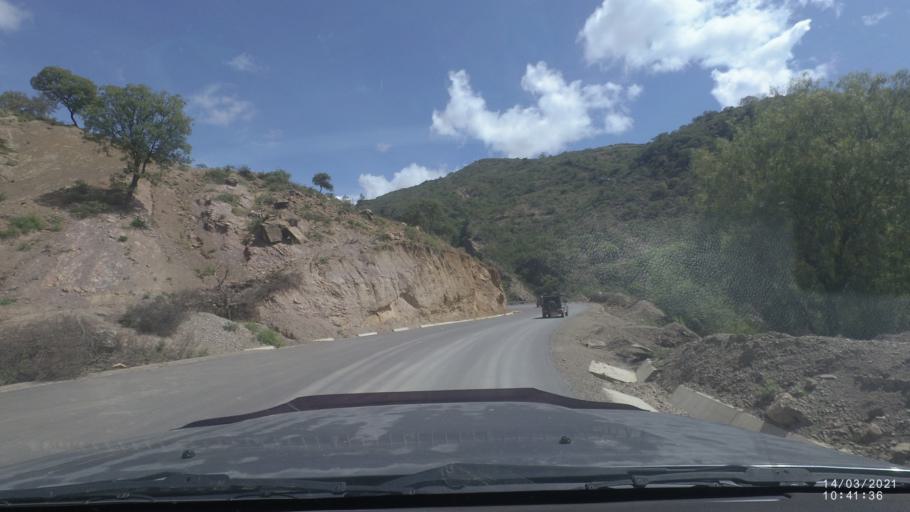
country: BO
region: Cochabamba
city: Tarata
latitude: -17.8792
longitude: -65.9128
